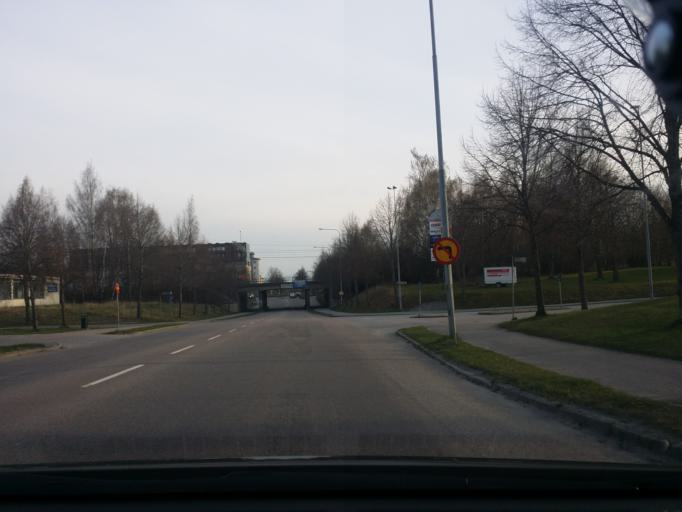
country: SE
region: Uppsala
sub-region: Enkopings Kommun
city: Enkoping
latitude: 59.6467
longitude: 17.0837
